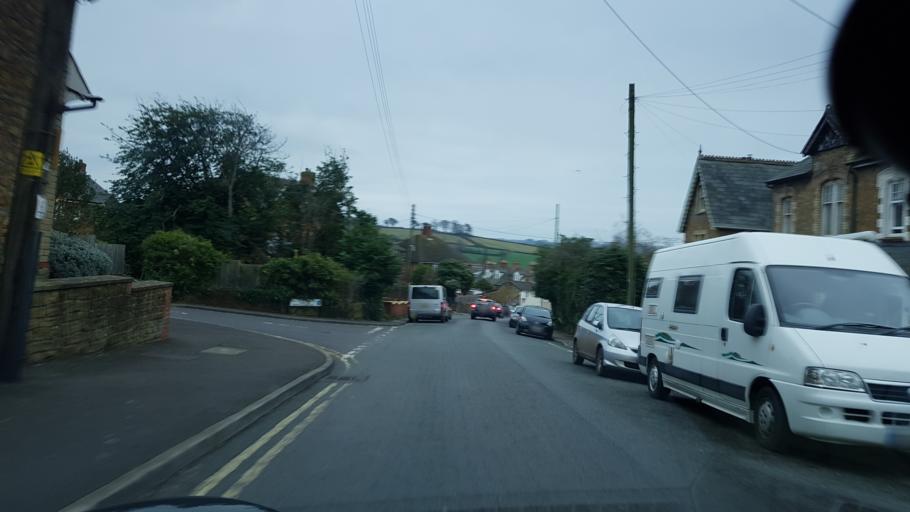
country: GB
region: England
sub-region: Somerset
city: Ilminster
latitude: 50.9295
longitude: -2.9160
